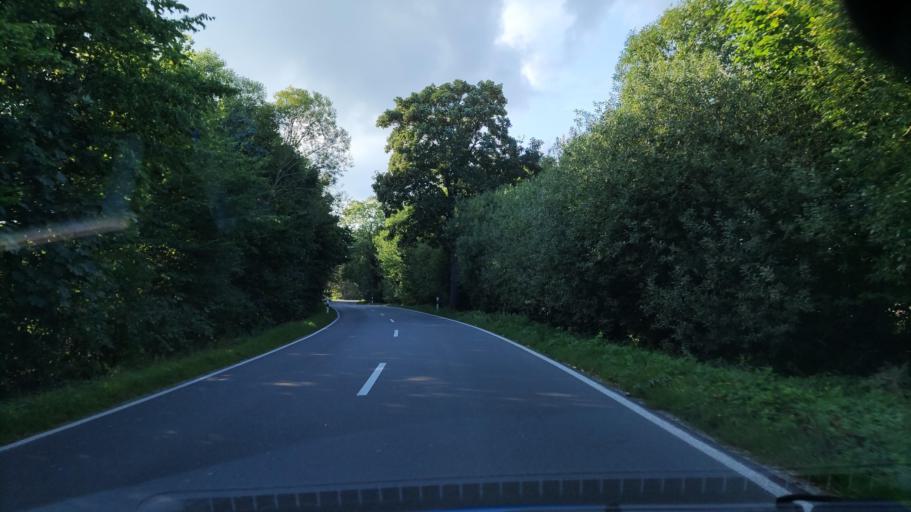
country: DE
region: Schleswig-Holstein
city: Ahrensbok
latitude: 54.0289
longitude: 10.5586
